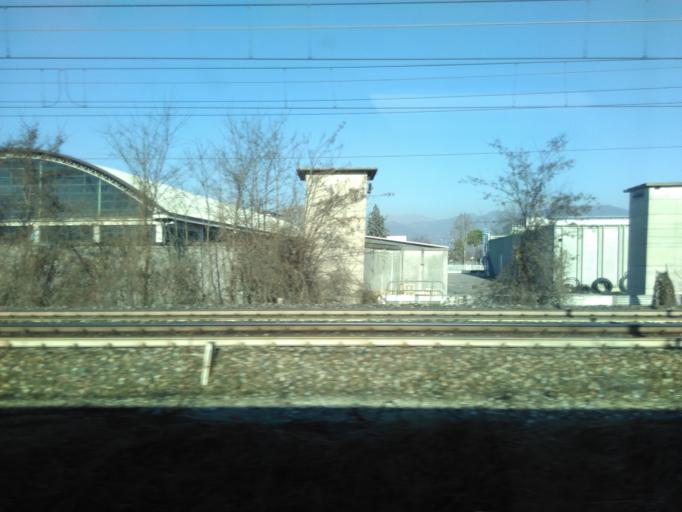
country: IT
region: Lombardy
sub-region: Provincia di Brescia
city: Castegnato
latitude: 45.5489
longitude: 10.1335
